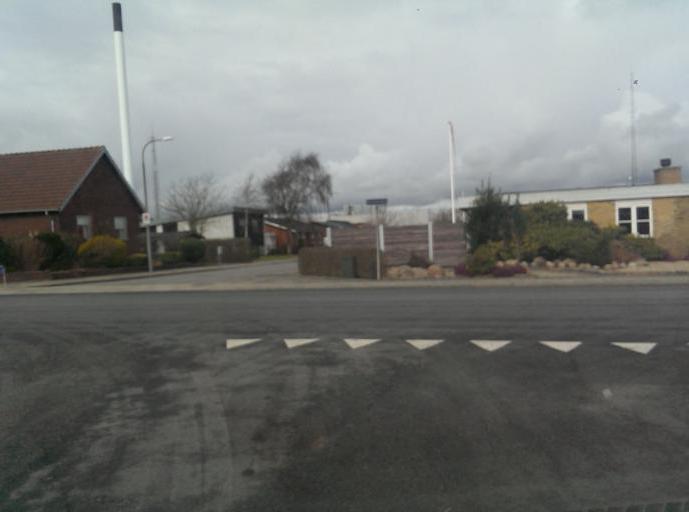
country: DK
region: South Denmark
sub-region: Esbjerg Kommune
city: Esbjerg
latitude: 55.5006
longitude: 8.4112
